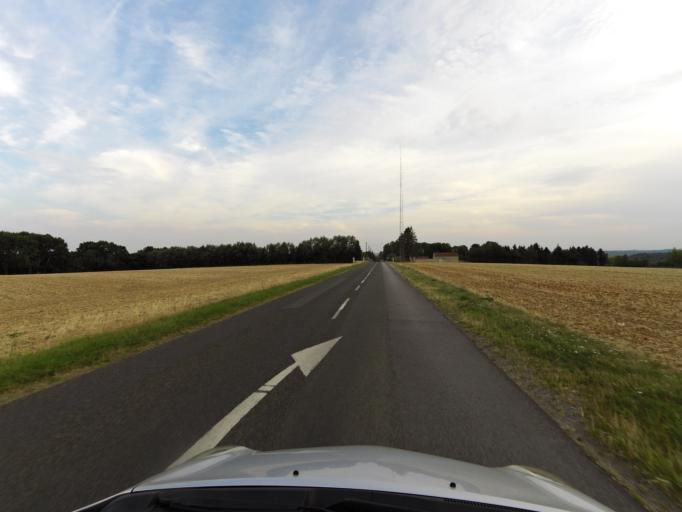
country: FR
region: Picardie
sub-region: Departement de l'Aisne
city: Bruyeres-et-Montberault
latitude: 49.4921
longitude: 3.6690
